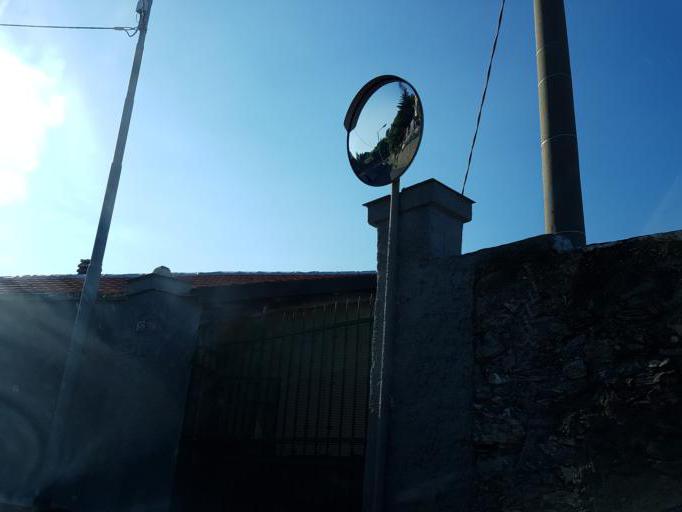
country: IT
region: Liguria
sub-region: Provincia di Genova
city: San Teodoro
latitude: 44.4279
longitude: 8.8715
